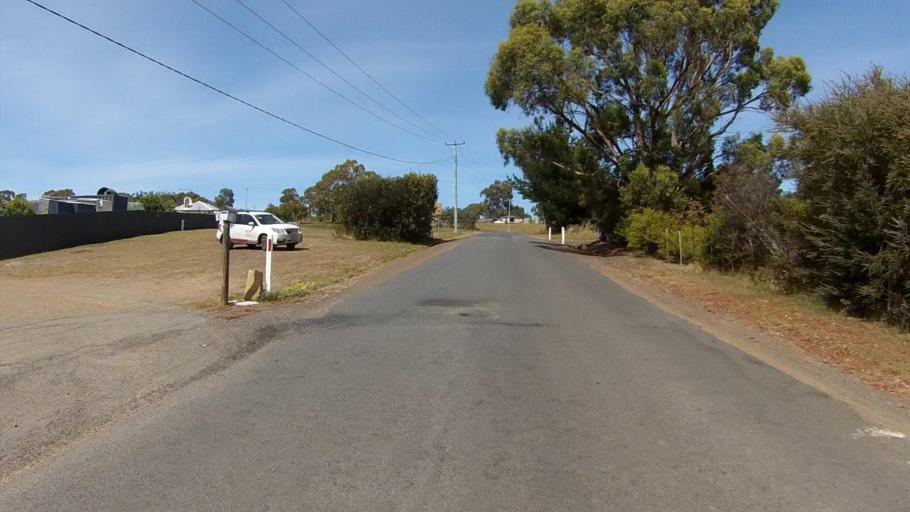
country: AU
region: Tasmania
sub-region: Sorell
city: Sorell
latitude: -42.6113
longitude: 147.7272
